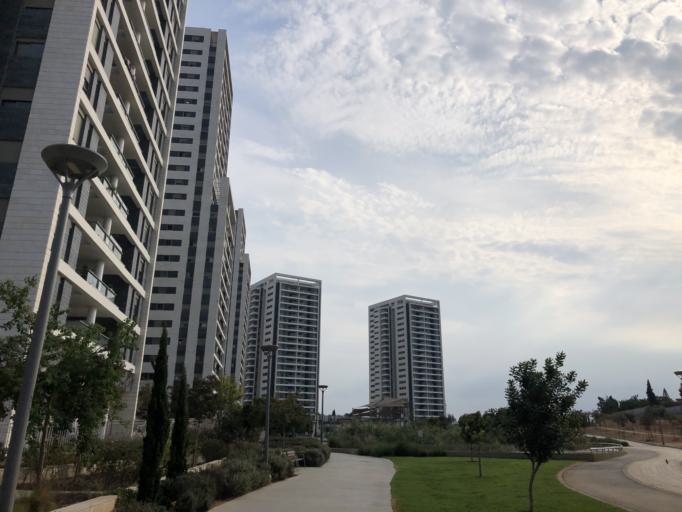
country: IL
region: Tel Aviv
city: Giv`at Shemu'el
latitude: 32.0571
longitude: 34.8452
